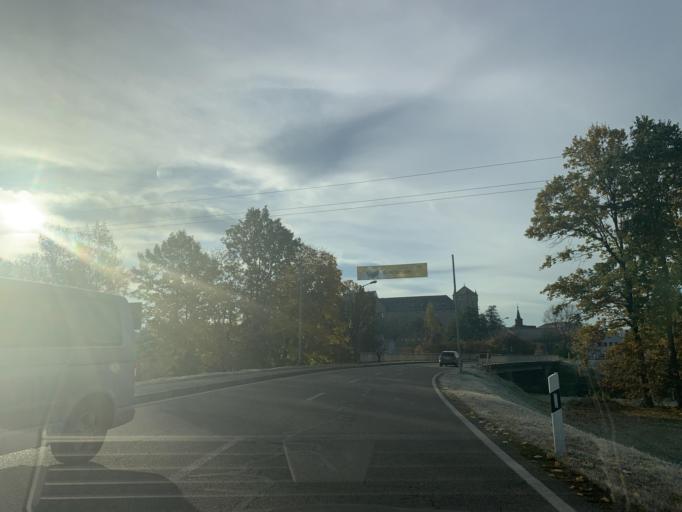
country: DE
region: Bavaria
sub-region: Upper Palatinate
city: Neunburg vorm Wald
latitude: 49.3515
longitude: 12.3827
